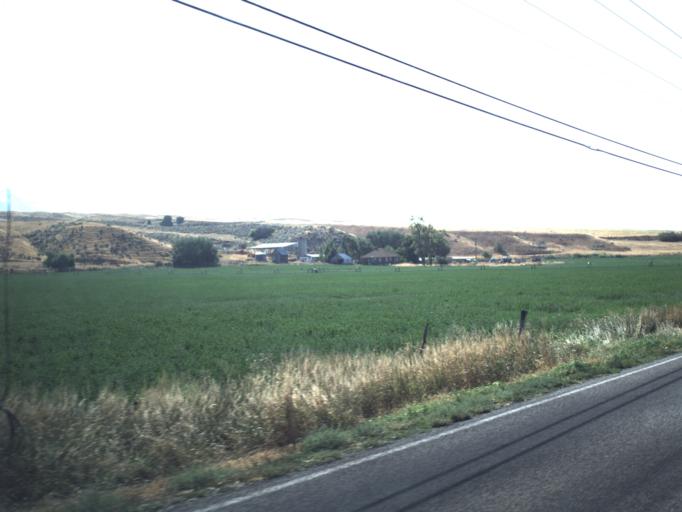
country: US
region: Utah
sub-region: Cache County
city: Hyrum
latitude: 41.6032
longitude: -111.8335
